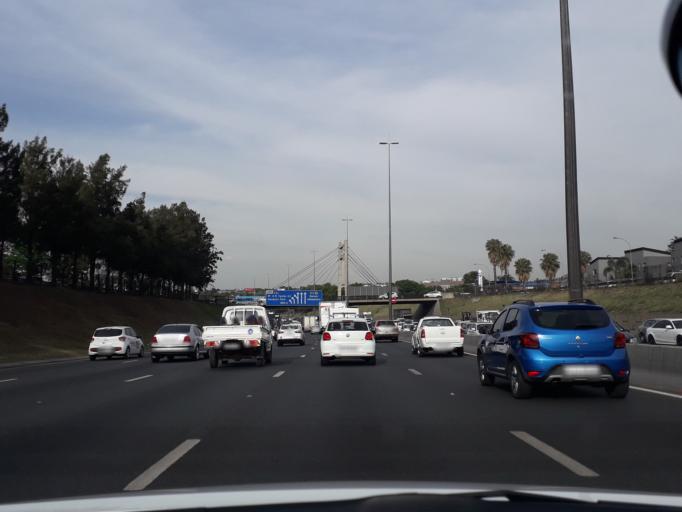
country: ZA
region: Gauteng
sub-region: Ekurhuleni Metropolitan Municipality
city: Germiston
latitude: -26.1662
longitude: 28.1431
